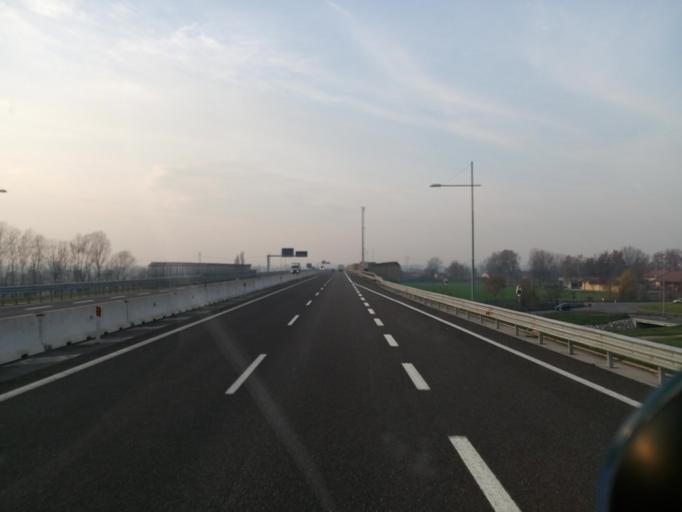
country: IT
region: Lombardy
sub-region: Provincia di Brescia
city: San Zeno Naviglio
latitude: 45.4670
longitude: 10.2098
